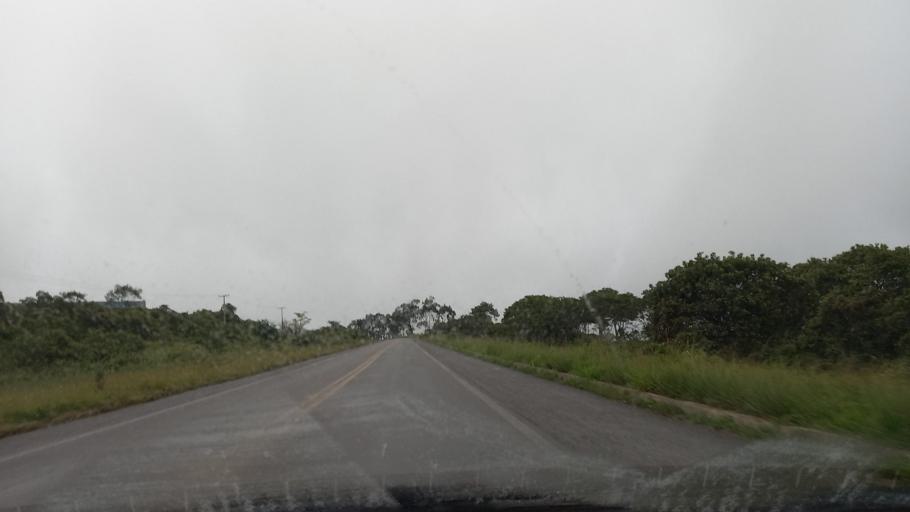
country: BR
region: Pernambuco
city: Garanhuns
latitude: -8.8728
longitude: -36.5342
